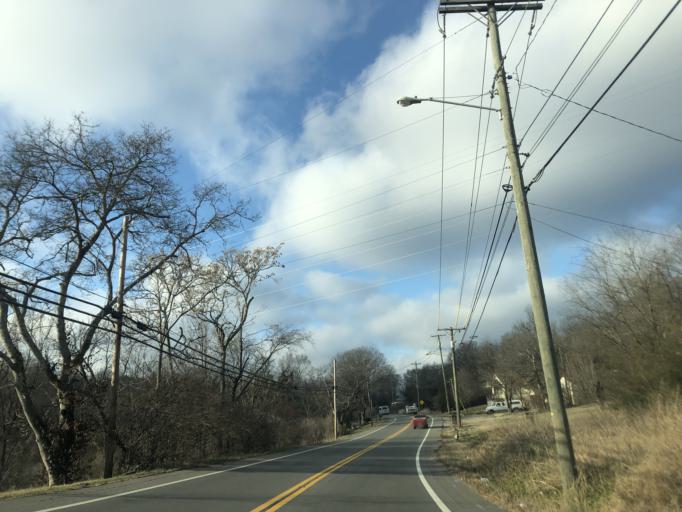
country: US
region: Tennessee
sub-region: Davidson County
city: Nashville
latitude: 36.2096
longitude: -86.7959
